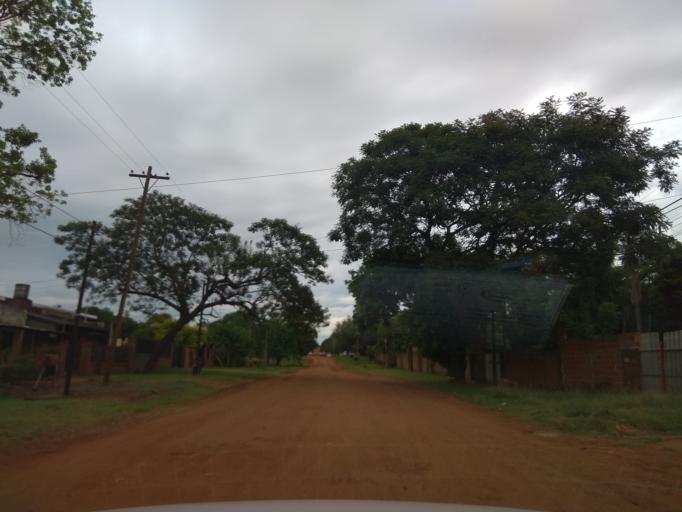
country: AR
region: Misiones
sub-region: Departamento de Capital
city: Posadas
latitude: -27.4101
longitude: -55.9061
